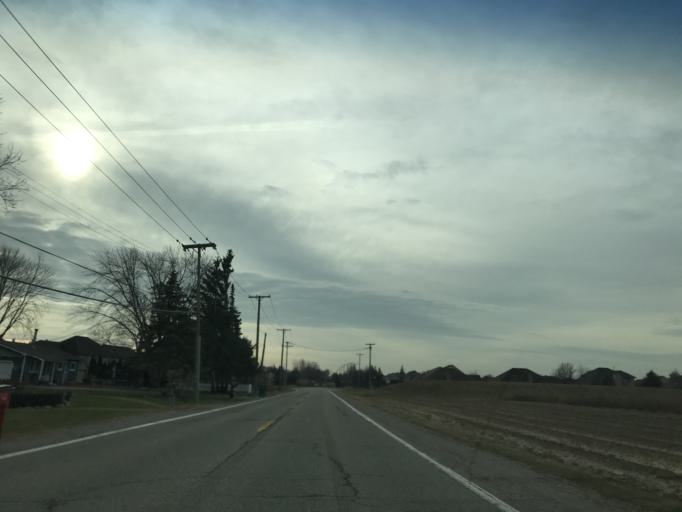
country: US
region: Michigan
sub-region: Macomb County
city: Shelby
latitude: 42.6995
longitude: -82.9589
